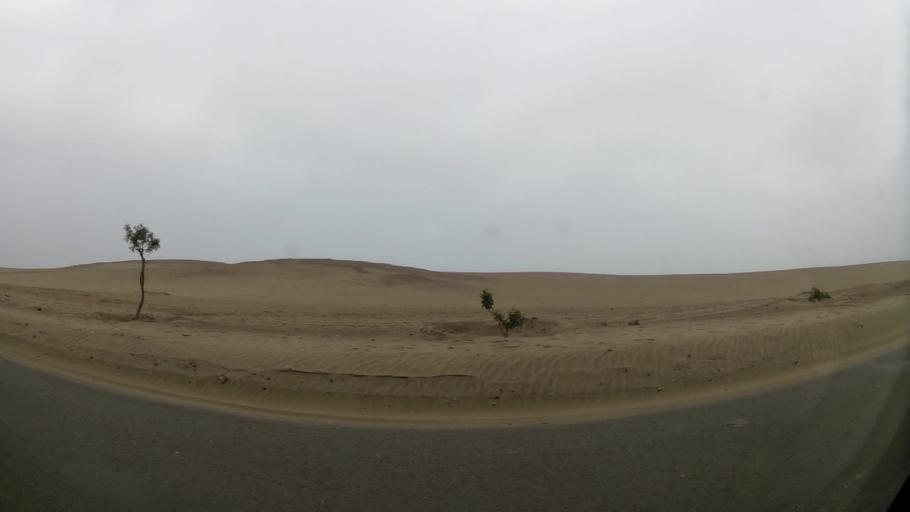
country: PE
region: Lima
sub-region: Lima
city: Punta Hermosa
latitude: -12.2452
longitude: -76.9087
